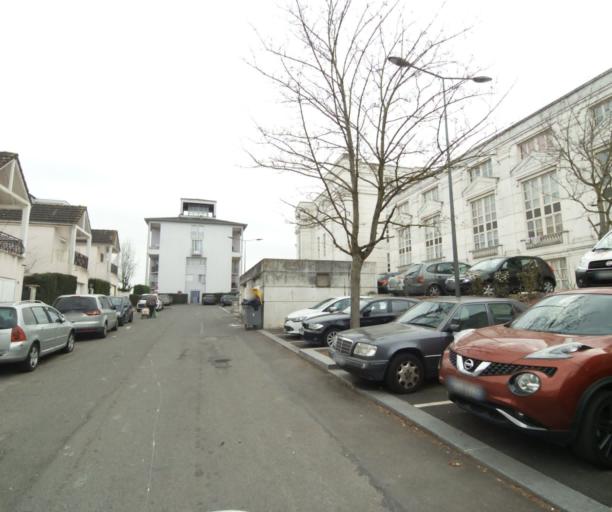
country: FR
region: Ile-de-France
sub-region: Departement du Val-d'Oise
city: Vaureal
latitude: 49.0464
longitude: 2.0349
